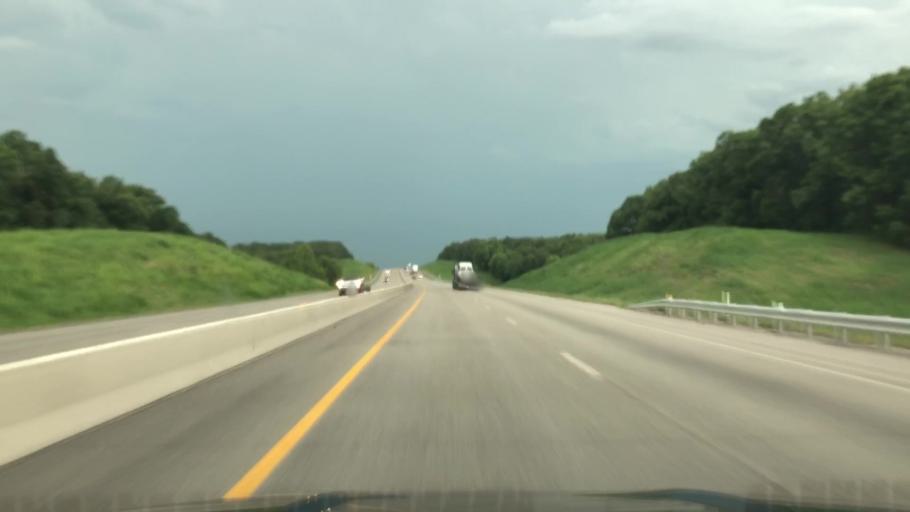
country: US
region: Oklahoma
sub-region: Rogers County
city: Justice
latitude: 36.3368
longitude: -95.5104
